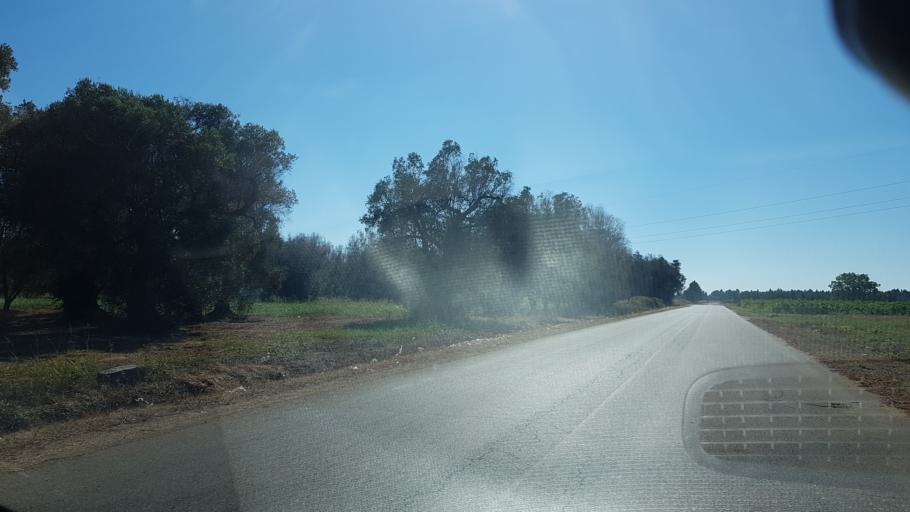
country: IT
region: Apulia
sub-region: Provincia di Brindisi
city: Mesagne
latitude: 40.5563
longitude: 17.8585
